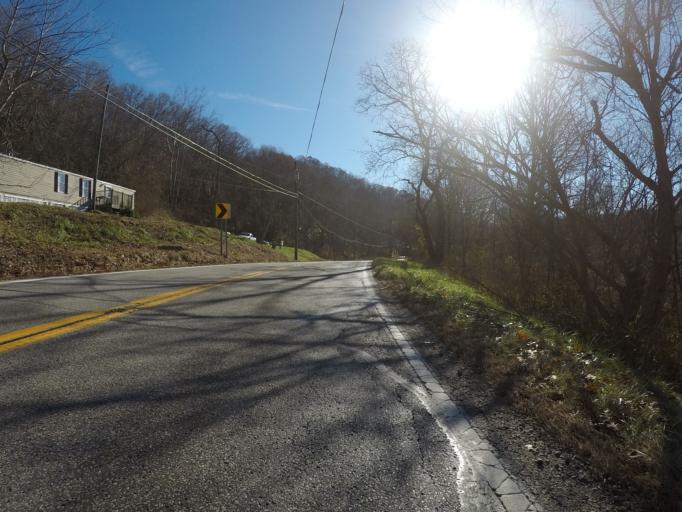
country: US
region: West Virginia
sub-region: Cabell County
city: Huntington
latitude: 38.4697
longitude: -82.4323
